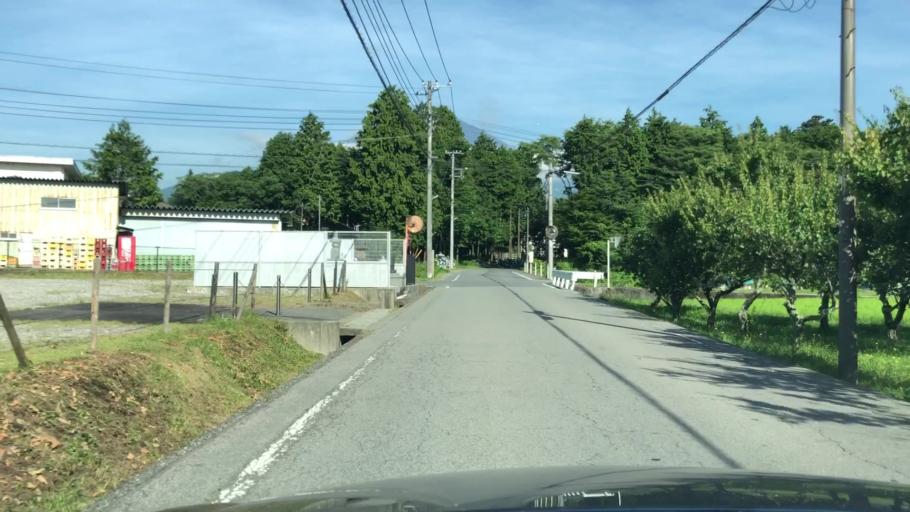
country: JP
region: Shizuoka
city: Gotemba
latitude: 35.3215
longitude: 138.9030
